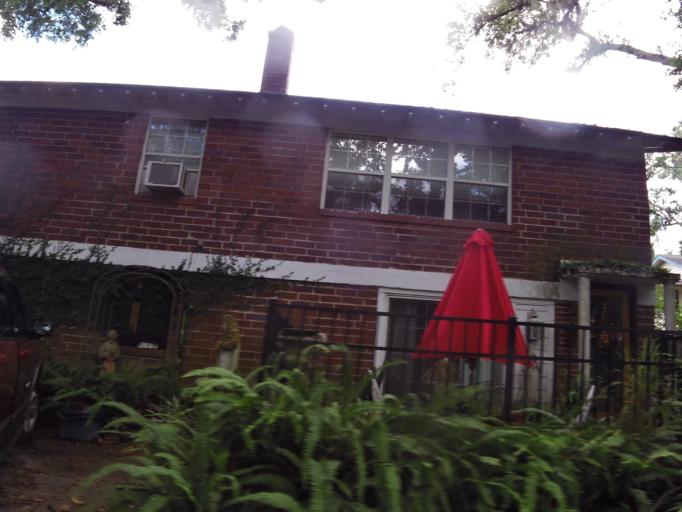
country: US
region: Florida
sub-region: Duval County
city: Jacksonville
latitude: 30.2905
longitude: -81.6468
